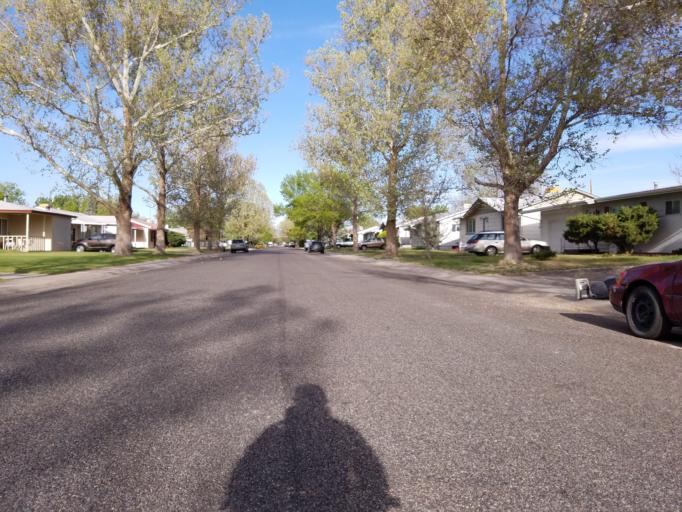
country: US
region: Colorado
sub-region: Mesa County
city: Grand Junction
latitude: 39.0828
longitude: -108.5350
